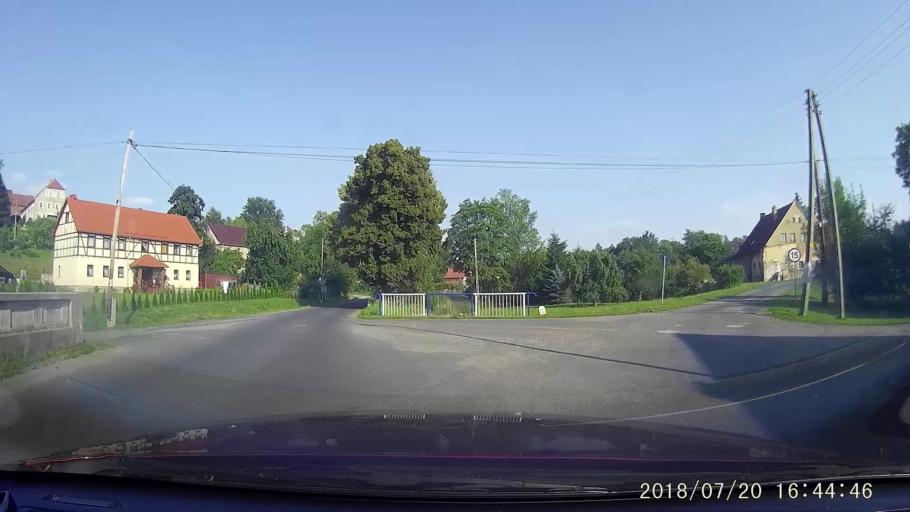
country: PL
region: Lower Silesian Voivodeship
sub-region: Powiat lubanski
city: Siekierczyn
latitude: 51.0672
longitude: 15.1680
